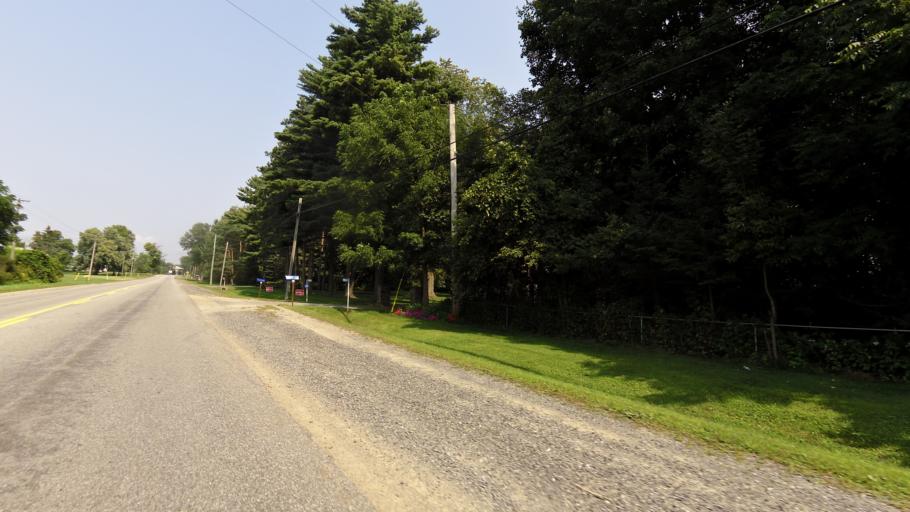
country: CA
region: Ontario
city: Brockville
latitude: 44.6456
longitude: -75.6009
